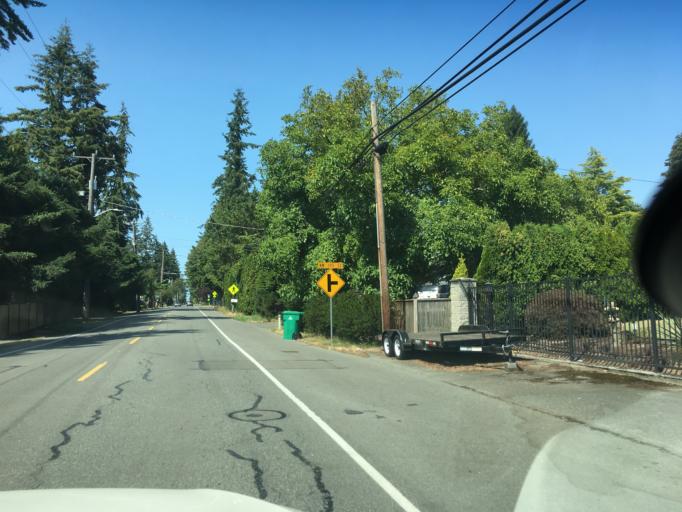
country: US
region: Washington
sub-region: Snohomish County
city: Esperance
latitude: 47.7691
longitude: -122.3666
